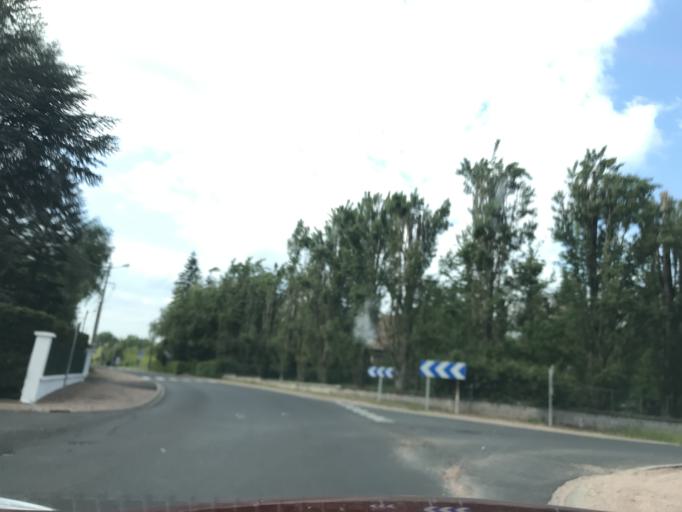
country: FR
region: Auvergne
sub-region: Departement du Puy-de-Dome
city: Lezoux
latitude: 45.8434
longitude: 3.3926
